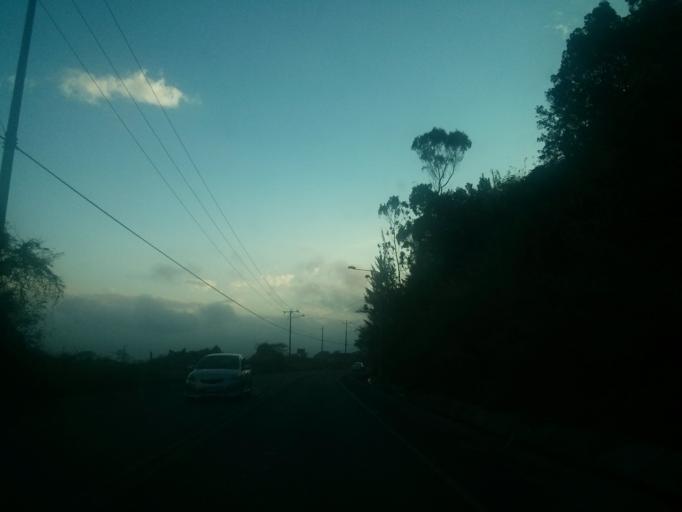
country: CR
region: Cartago
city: Cartago
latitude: 9.8782
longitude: -83.9039
